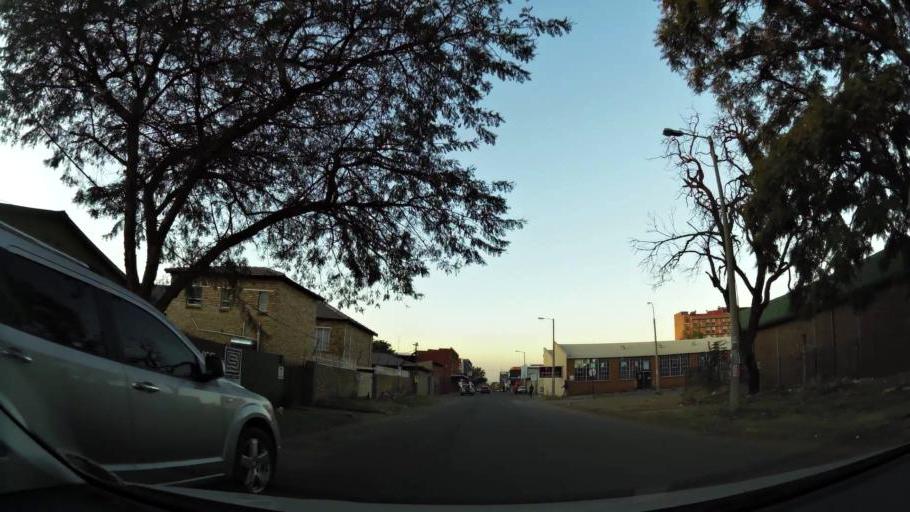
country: ZA
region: North-West
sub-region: Bojanala Platinum District Municipality
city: Rustenburg
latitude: -25.6718
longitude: 27.2408
